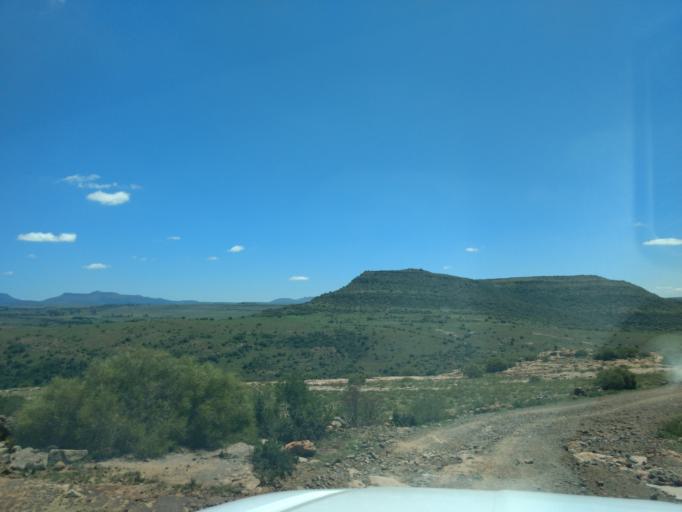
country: LS
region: Maseru
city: Maseru
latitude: -29.4540
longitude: 27.3681
